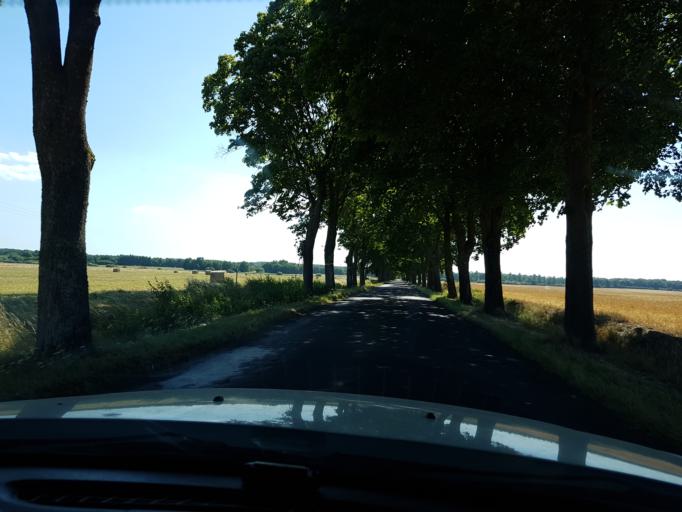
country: PL
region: West Pomeranian Voivodeship
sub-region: Powiat bialogardzki
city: Bialogard
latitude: 53.9831
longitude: 15.9278
